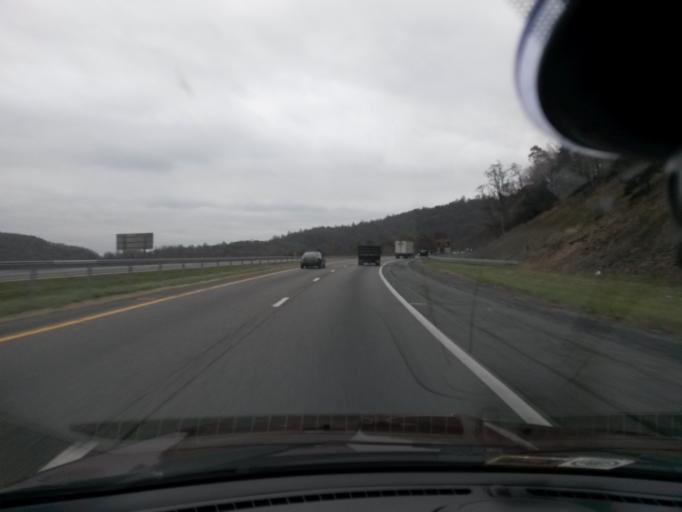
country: US
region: Virginia
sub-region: City of Waynesboro
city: Waynesboro
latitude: 38.0392
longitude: -78.8724
